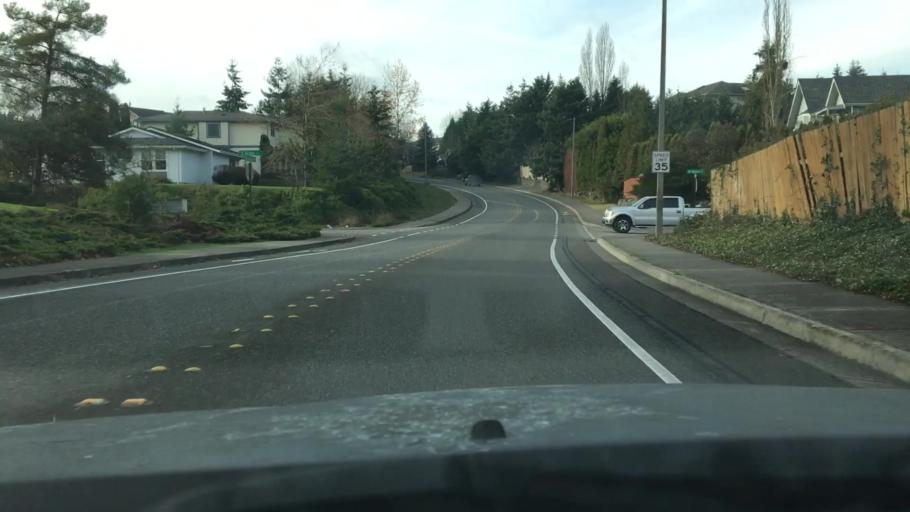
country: US
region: Washington
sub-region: Whatcom County
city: Geneva
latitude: 48.7725
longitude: -122.4110
